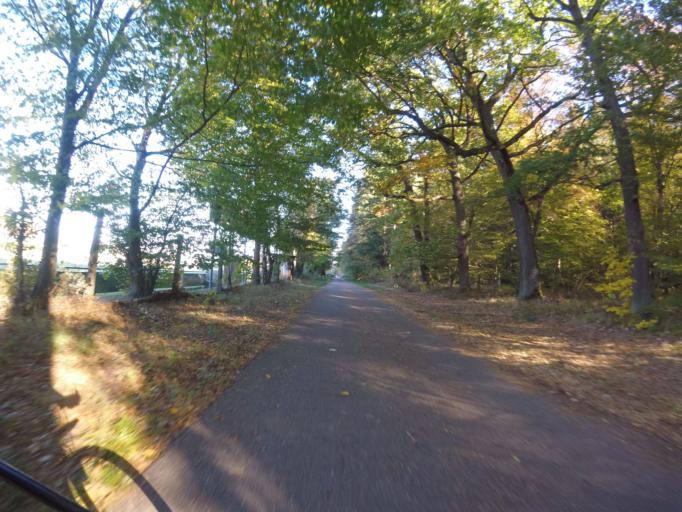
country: DE
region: Baden-Wuerttemberg
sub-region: Karlsruhe Region
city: Eggenstein-Leopoldshafen
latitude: 49.0733
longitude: 8.4106
